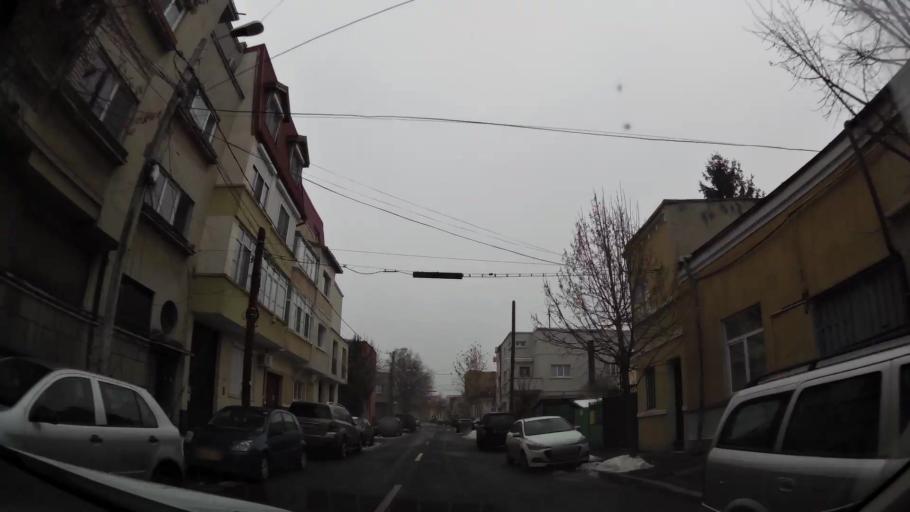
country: RO
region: Bucuresti
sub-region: Municipiul Bucuresti
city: Bucharest
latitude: 44.4359
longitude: 26.1291
